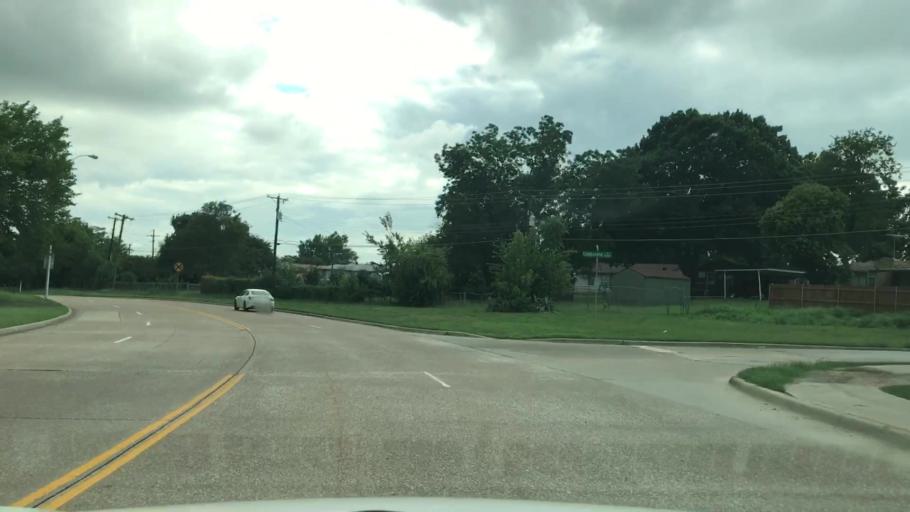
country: US
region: Texas
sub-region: Dallas County
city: Richardson
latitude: 32.9176
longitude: -96.7541
